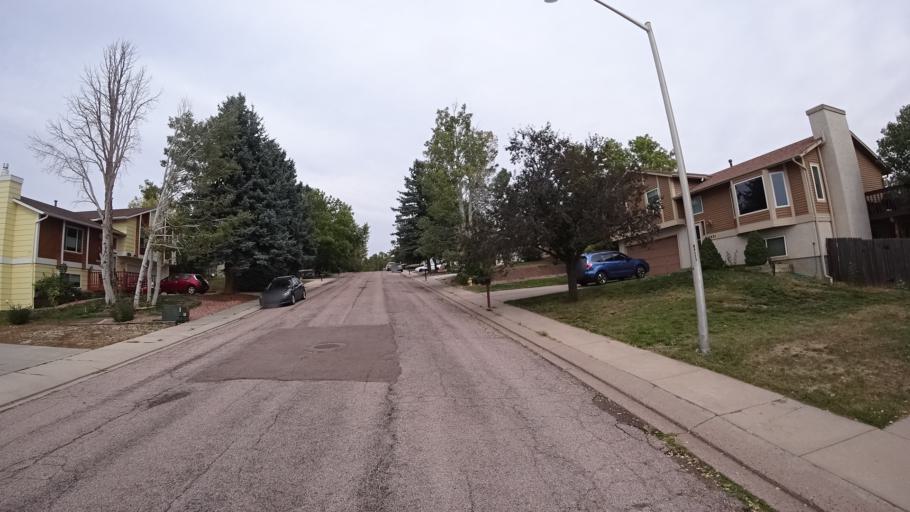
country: US
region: Colorado
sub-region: El Paso County
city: Cimarron Hills
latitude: 38.9041
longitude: -104.7267
